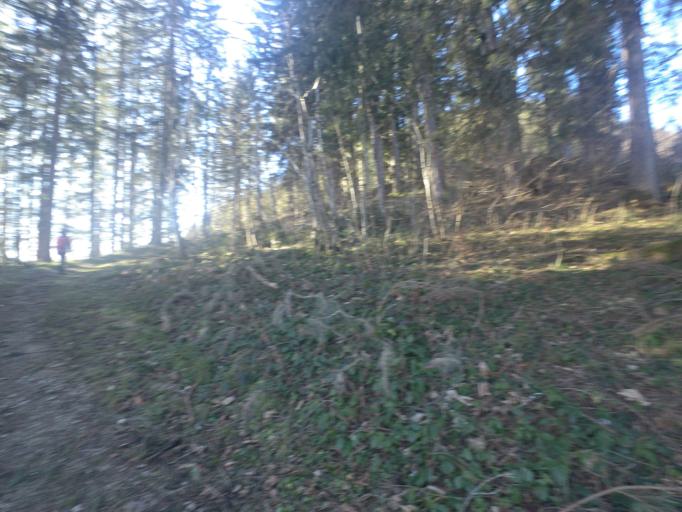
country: AT
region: Salzburg
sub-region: Politischer Bezirk Hallein
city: Abtenau
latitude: 47.5972
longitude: 13.4611
